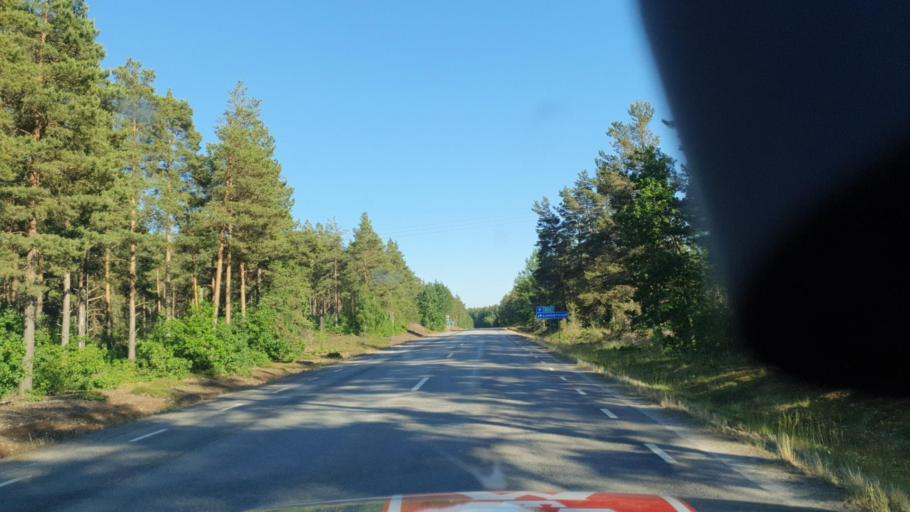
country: SE
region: Kalmar
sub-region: Kalmar Kommun
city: Ljungbyholm
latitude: 56.6472
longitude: 16.1644
